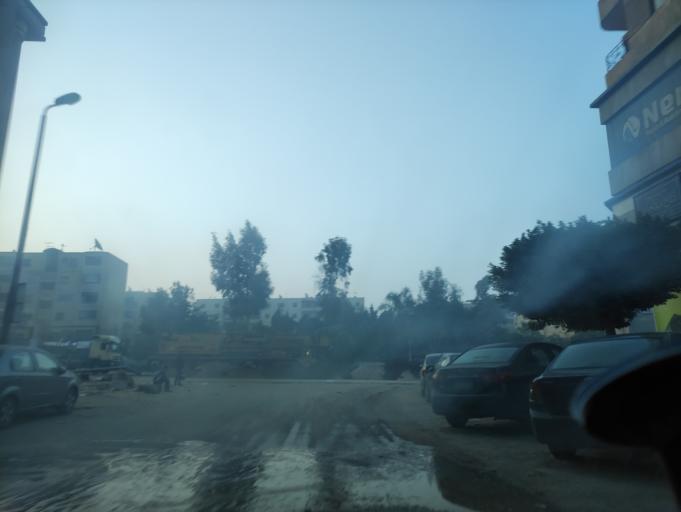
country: EG
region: Muhafazat al Qahirah
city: Cairo
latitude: 30.0484
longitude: 31.3691
